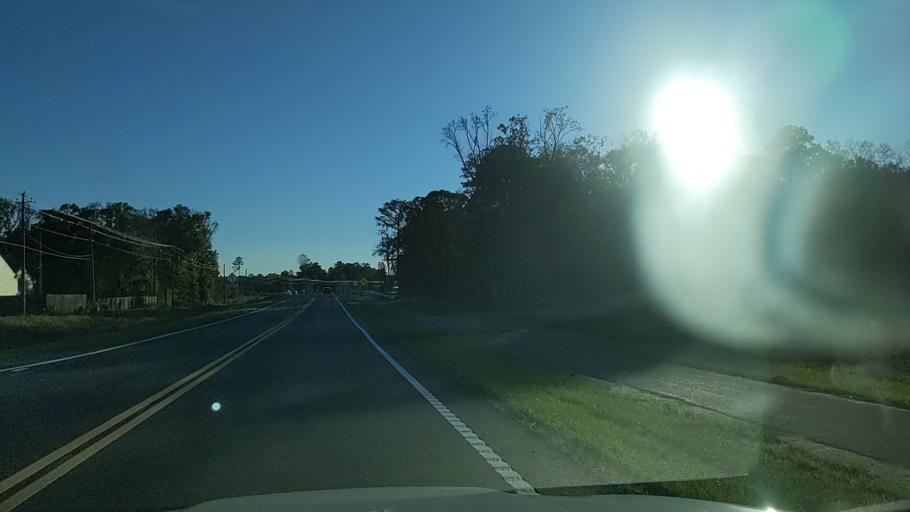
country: US
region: Georgia
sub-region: Chatham County
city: Port Wentworth
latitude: 32.1835
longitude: -81.2231
